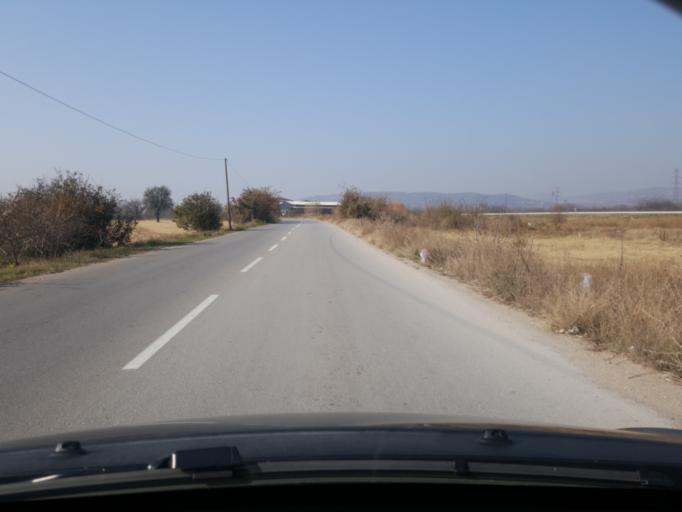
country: RS
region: Central Serbia
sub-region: Nisavski Okrug
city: Niska Banja
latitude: 43.3266
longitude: 21.9622
